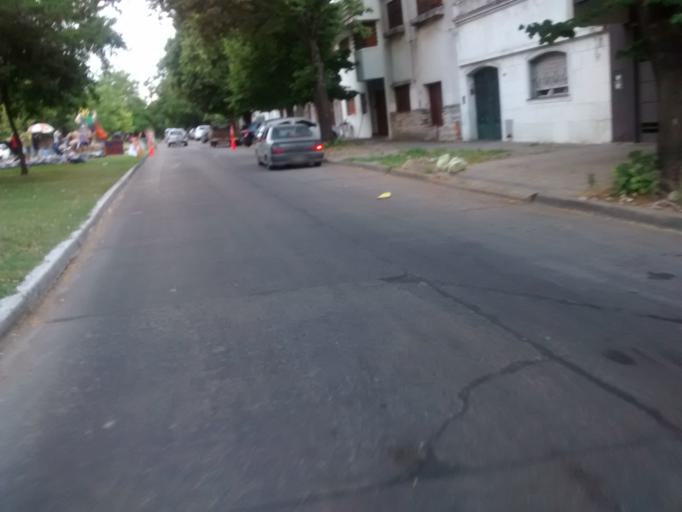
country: AR
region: Buenos Aires
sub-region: Partido de La Plata
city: La Plata
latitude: -34.9354
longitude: -57.9493
